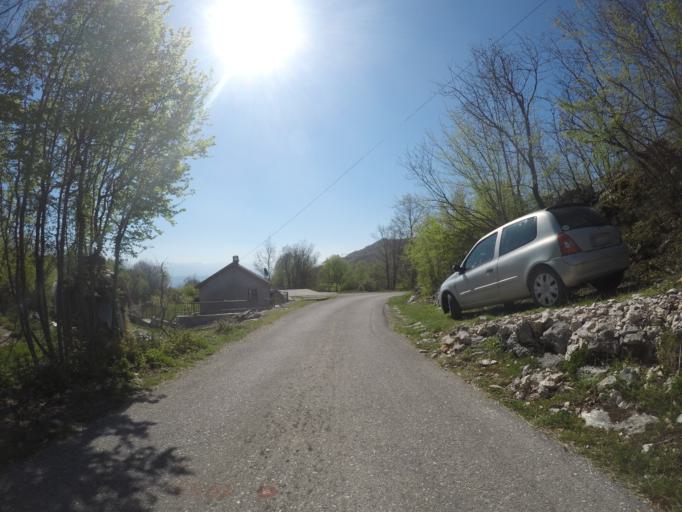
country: ME
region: Danilovgrad
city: Danilovgrad
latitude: 42.5176
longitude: 19.0525
